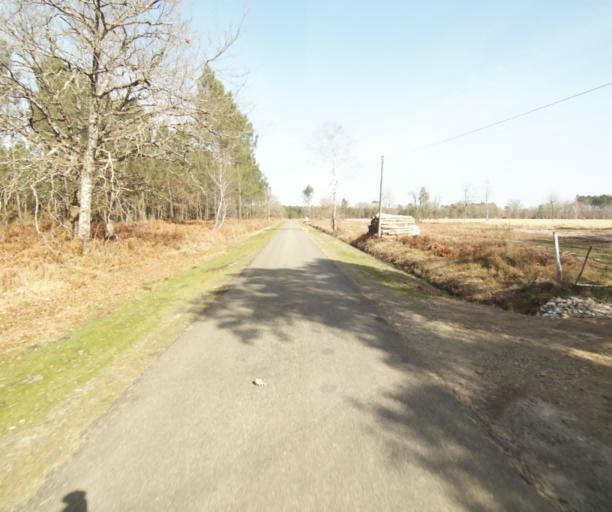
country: FR
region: Aquitaine
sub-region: Departement des Landes
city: Roquefort
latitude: 44.1559
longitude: -0.2275
